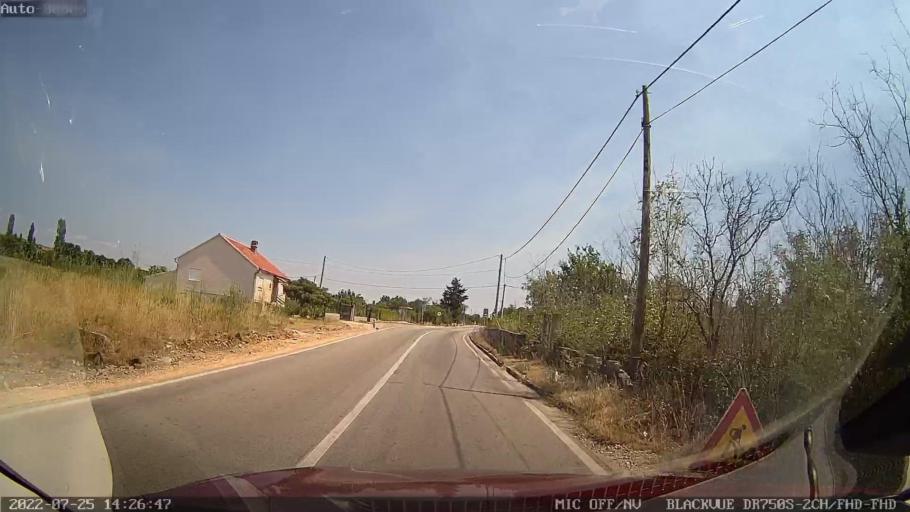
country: HR
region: Zadarska
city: Policnik
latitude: 44.1369
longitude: 15.3405
